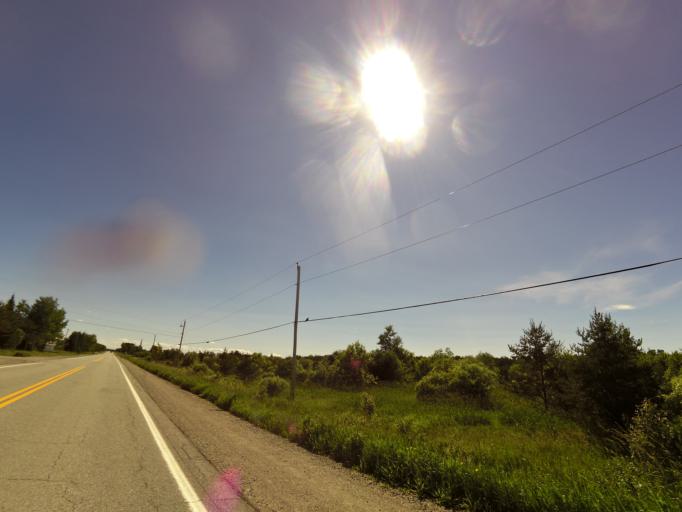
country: CA
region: Quebec
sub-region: Abitibi-Temiscamingue
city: Senneterre
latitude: 48.2665
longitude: -77.3245
